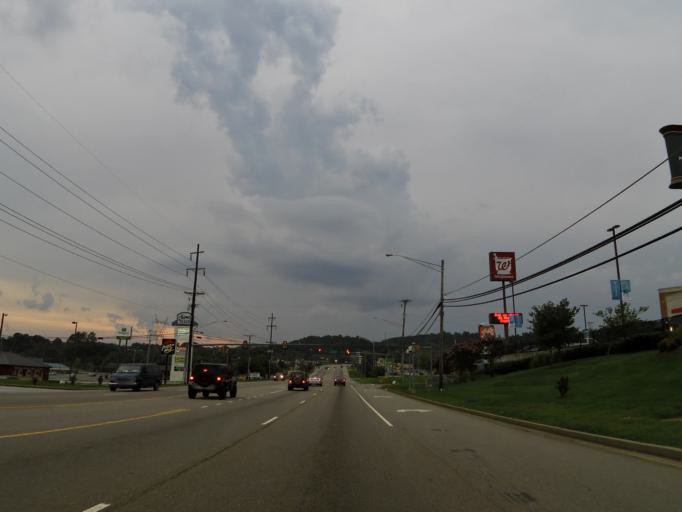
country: US
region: Tennessee
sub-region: Knox County
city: Knoxville
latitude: 35.9088
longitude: -83.8459
